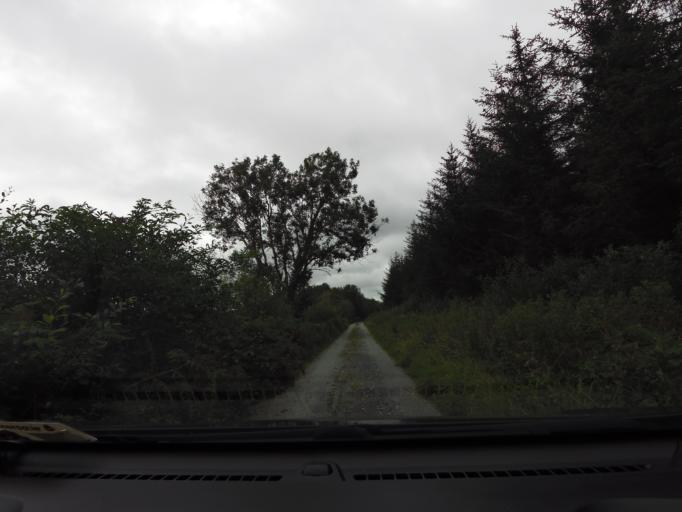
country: IE
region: Connaught
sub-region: County Galway
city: Athenry
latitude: 53.3007
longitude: -8.6674
